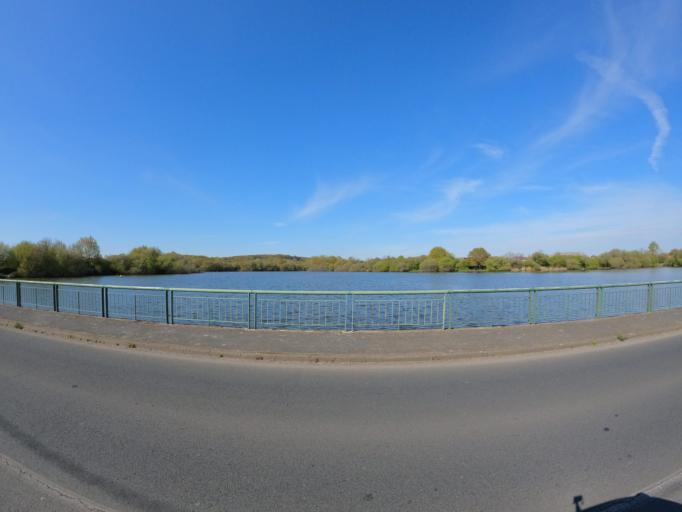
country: FR
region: Pays de la Loire
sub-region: Departement de Maine-et-Loire
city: Cholet
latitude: 47.0692
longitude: -0.9080
